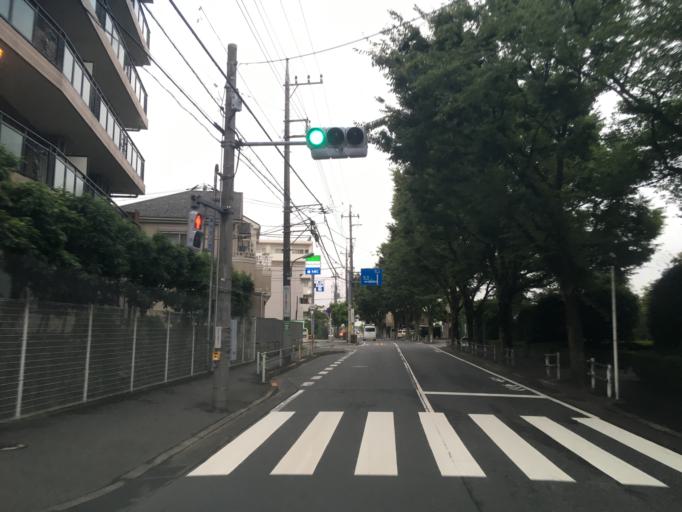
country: JP
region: Tokyo
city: Chofugaoka
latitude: 35.6384
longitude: 139.5527
